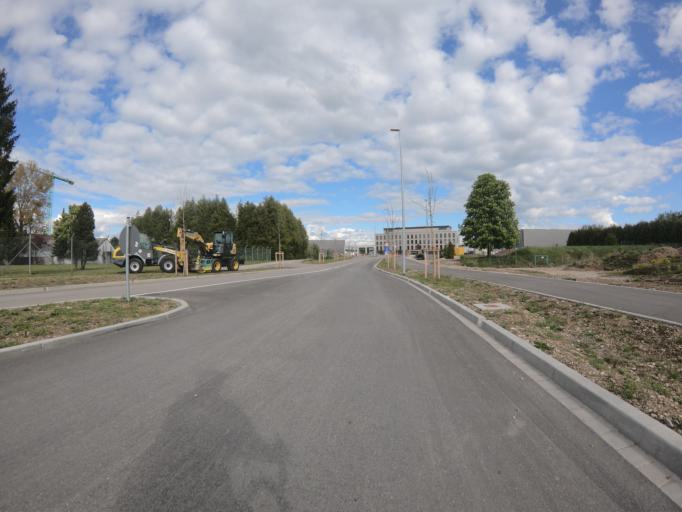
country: DE
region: Bavaria
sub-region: Upper Bavaria
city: Gilching
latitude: 48.0894
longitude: 11.2823
